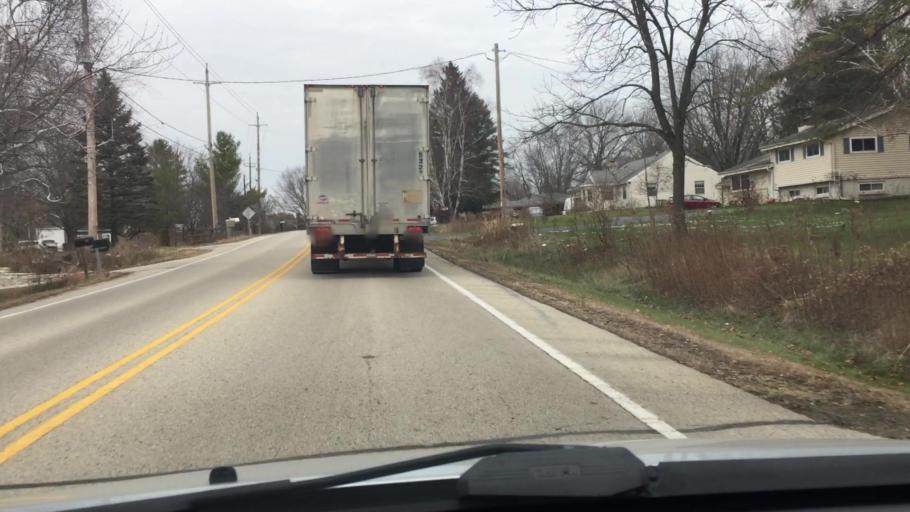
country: US
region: Wisconsin
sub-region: Ozaukee County
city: Grafton
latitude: 43.2953
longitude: -87.9604
